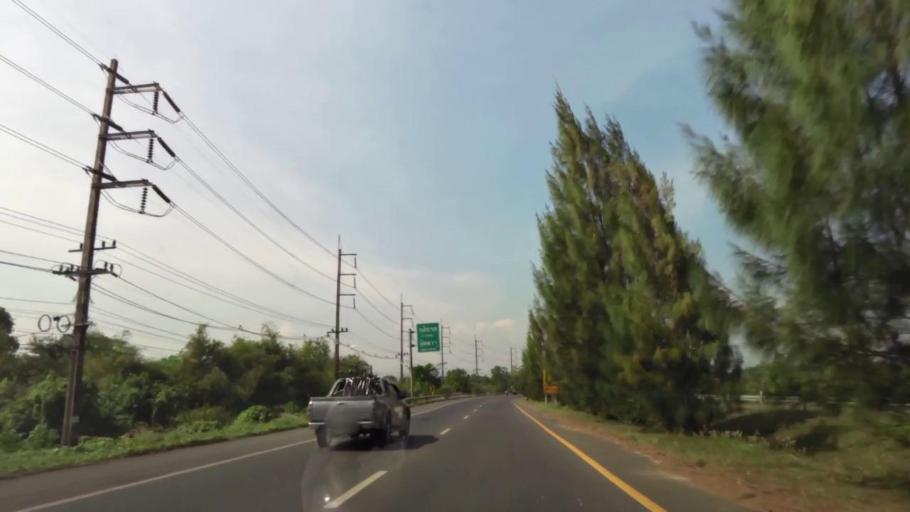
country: TH
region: Chanthaburi
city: Chanthaburi
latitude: 12.6415
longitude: 102.1322
